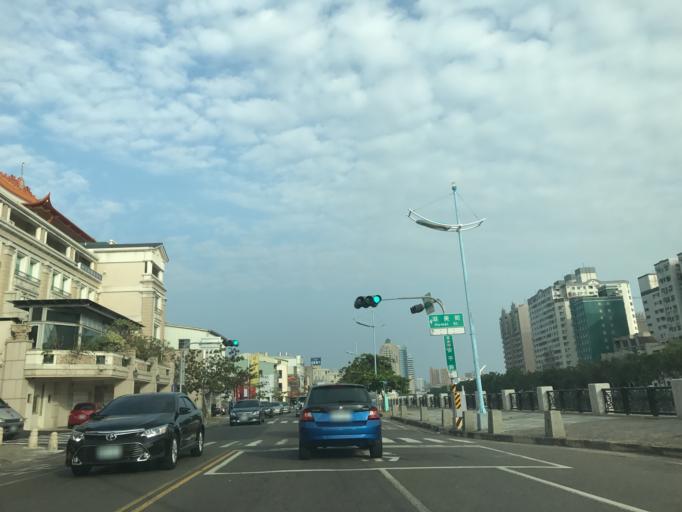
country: TW
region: Taiwan
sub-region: Tainan
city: Tainan
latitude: 22.9984
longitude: 120.1799
